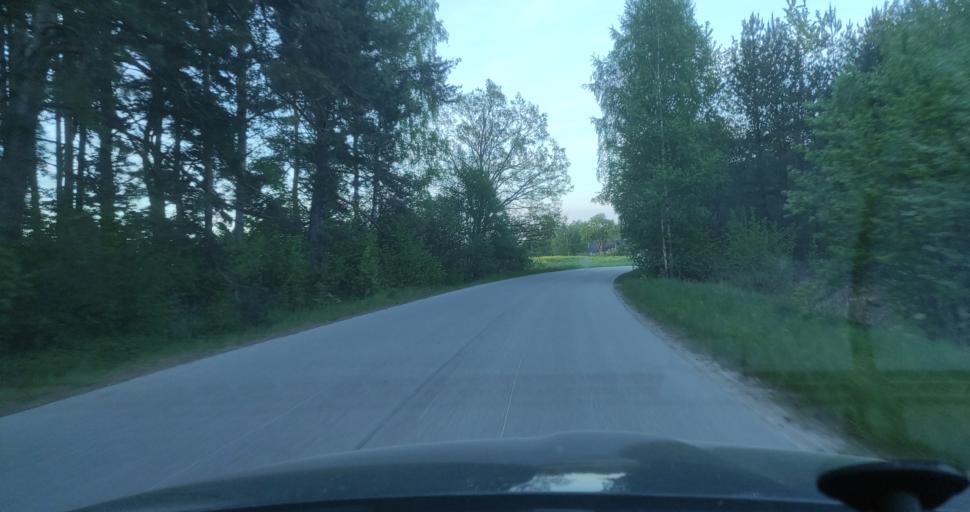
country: LV
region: Kuldigas Rajons
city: Kuldiga
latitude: 56.9565
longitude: 21.9412
